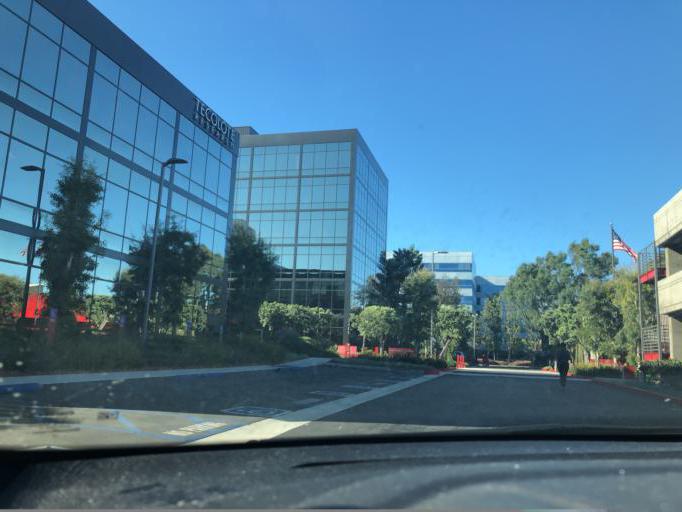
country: US
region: California
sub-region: Los Angeles County
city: Del Aire
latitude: 33.9185
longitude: -118.3896
